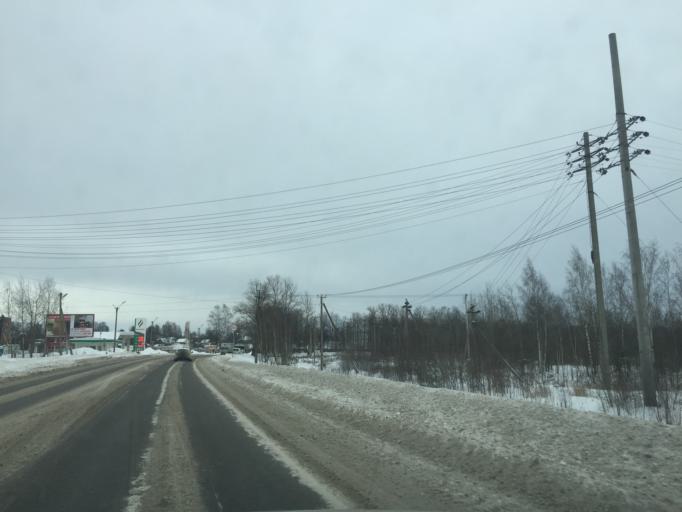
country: RU
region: Leningrad
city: Yanino Vtoroye
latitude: 59.9441
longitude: 30.6014
